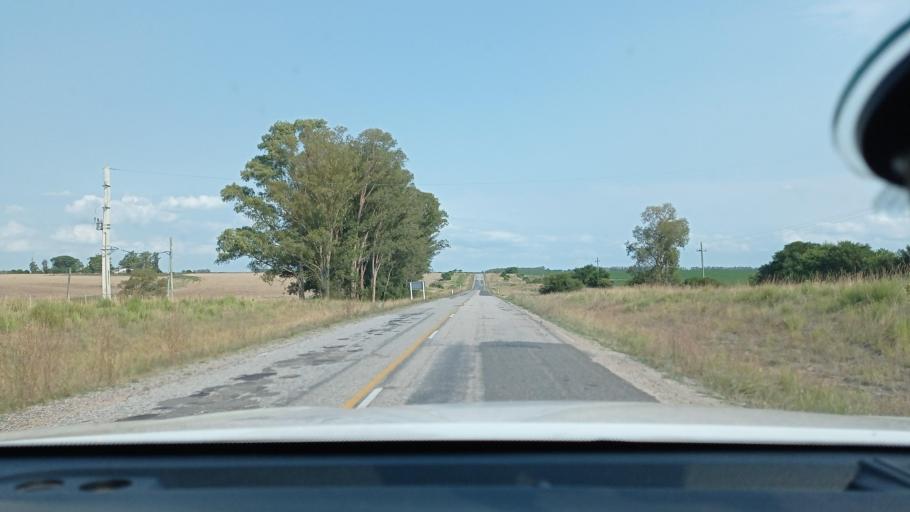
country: UY
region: Canelones
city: San Ramon
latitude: -34.1908
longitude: -56.0576
